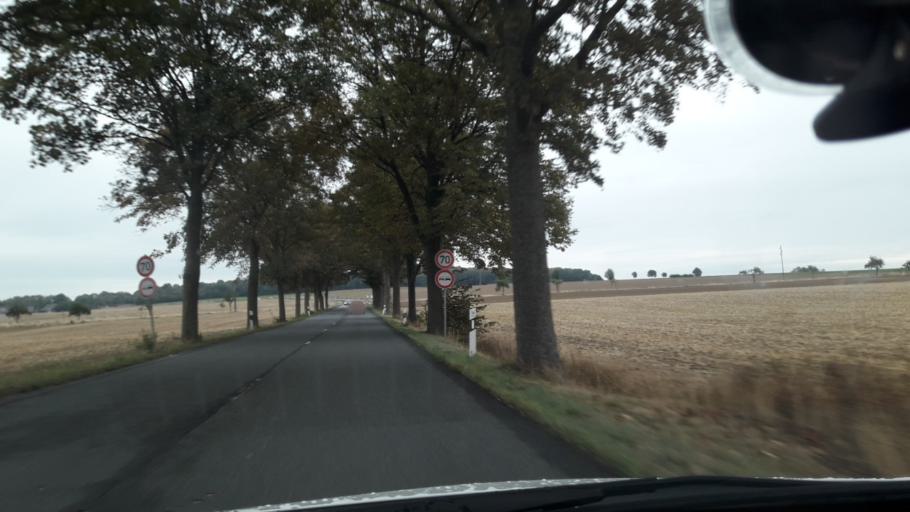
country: DE
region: Lower Saxony
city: Gielde
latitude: 52.0209
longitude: 10.4966
